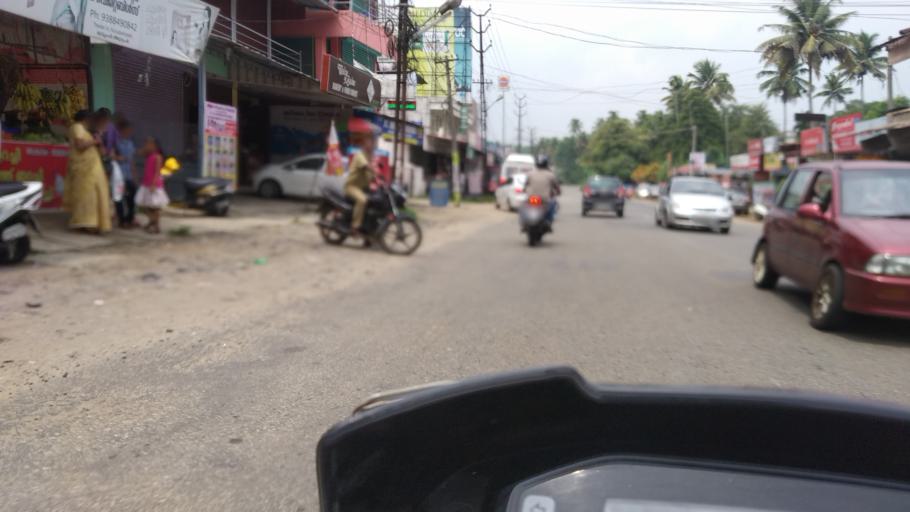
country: IN
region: Kerala
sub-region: Ernakulam
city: Perumpavur
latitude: 10.1126
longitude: 76.5132
